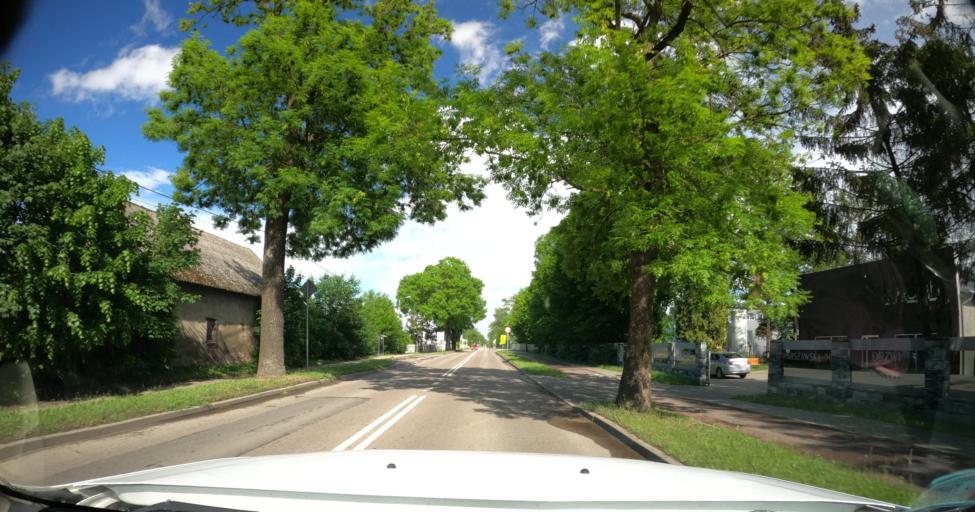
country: PL
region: Pomeranian Voivodeship
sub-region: Powiat nowodworski
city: Nowy Dwor Gdanski
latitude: 54.2089
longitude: 19.1302
